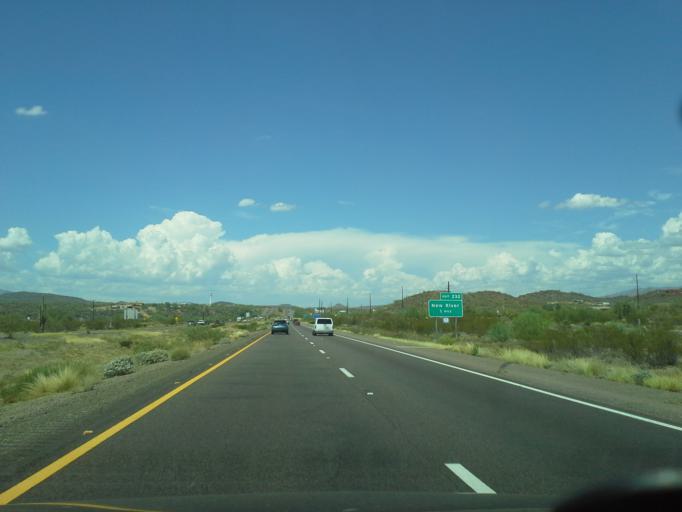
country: US
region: Arizona
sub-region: Maricopa County
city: New River
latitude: 33.8974
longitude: -112.1467
